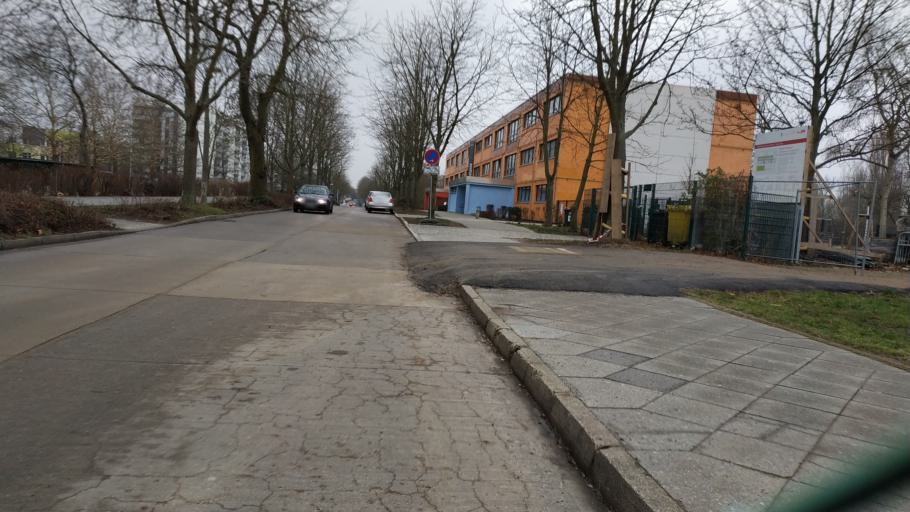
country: DE
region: Berlin
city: Hellersdorf
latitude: 52.5408
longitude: 13.6001
